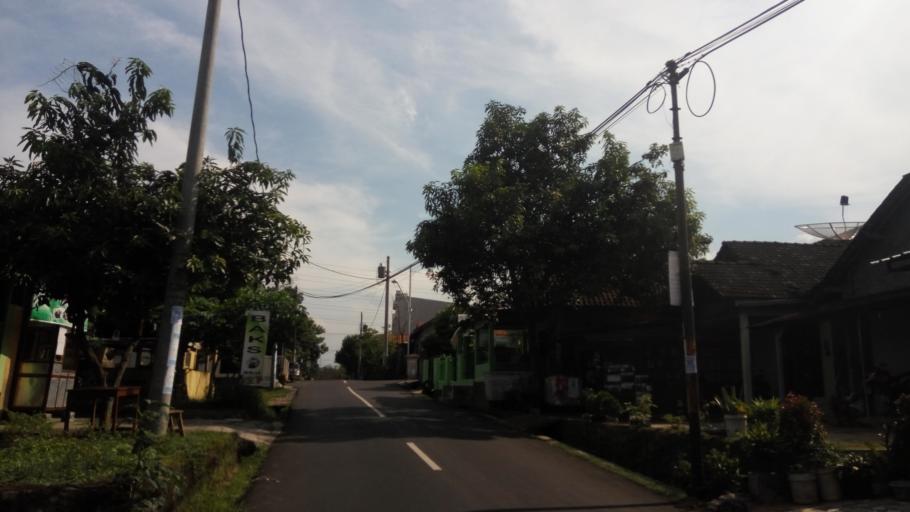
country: ID
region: Central Java
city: Ungaran
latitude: -7.1487
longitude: 110.4218
